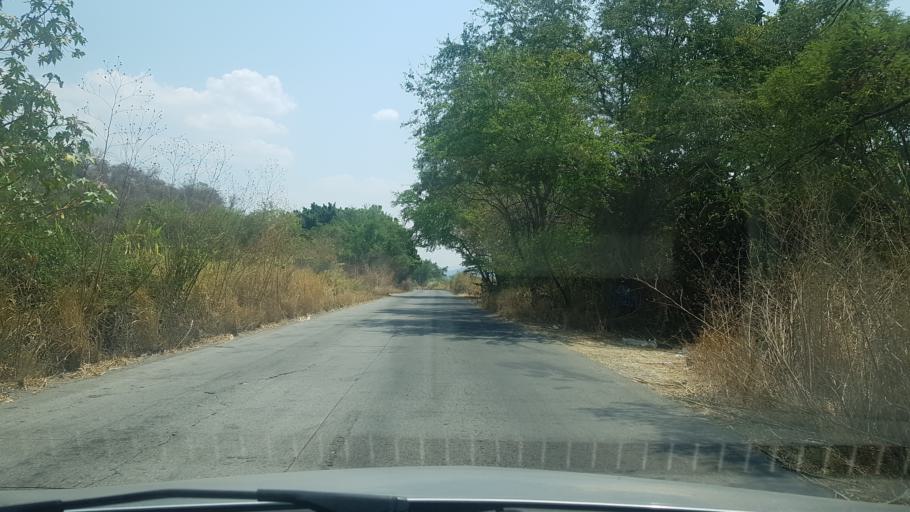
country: MX
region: Morelos
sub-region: Jiutepec
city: Independencia
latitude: 18.7924
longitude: -99.1035
